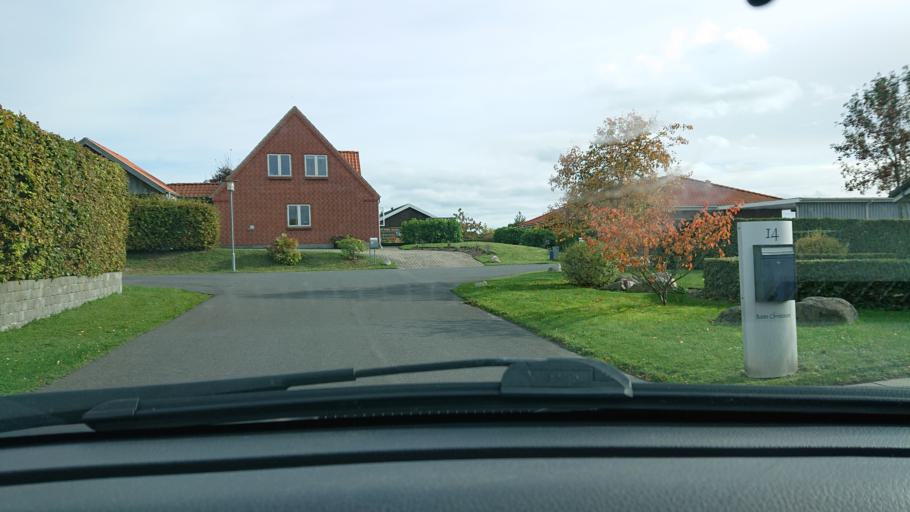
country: DK
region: South Denmark
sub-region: Nyborg Kommune
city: Nyborg
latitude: 55.3066
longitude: 10.7643
